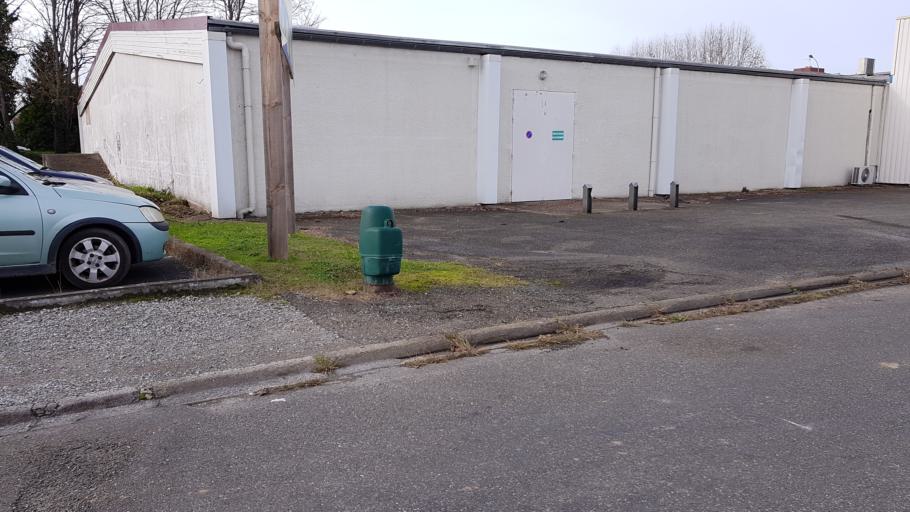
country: FR
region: Aquitaine
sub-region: Departement des Landes
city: Saint-Paul-les-Dax
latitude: 43.7257
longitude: -1.0765
